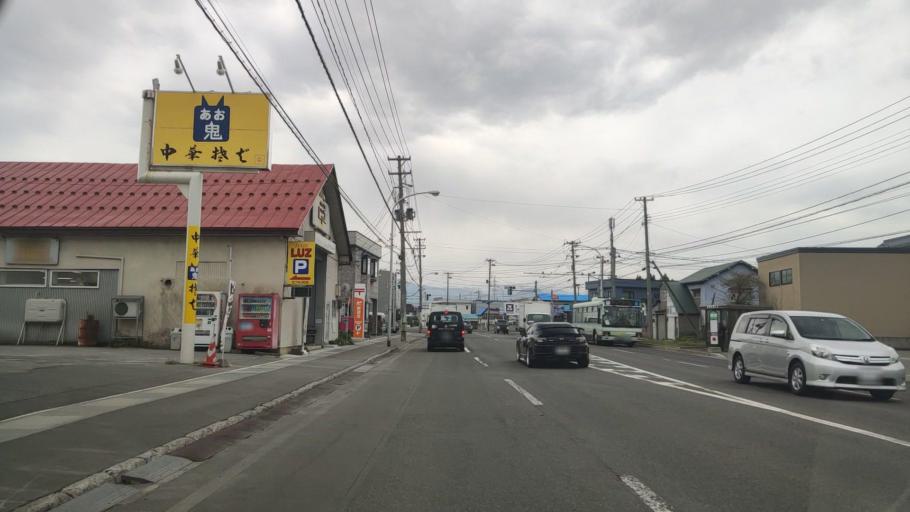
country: JP
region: Aomori
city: Aomori Shi
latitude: 40.8142
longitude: 140.7761
